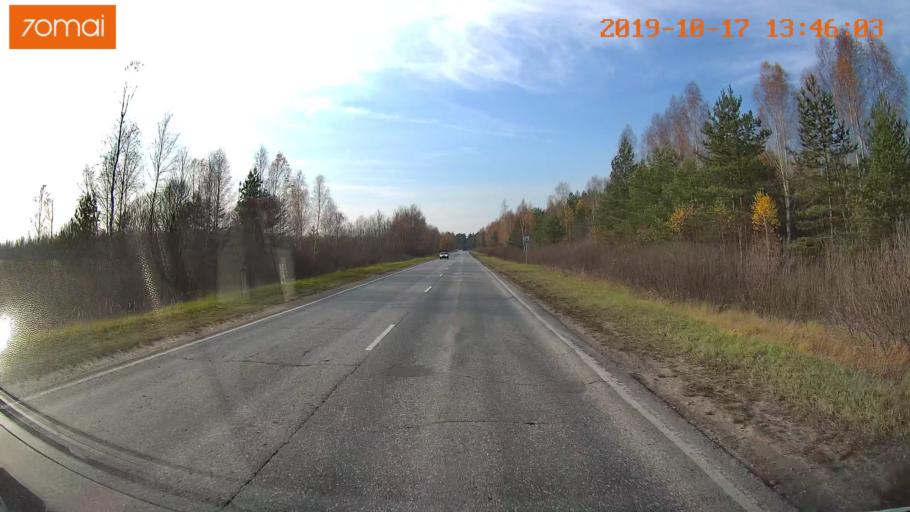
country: RU
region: Rjazan
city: Tuma
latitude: 55.1474
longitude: 40.4995
